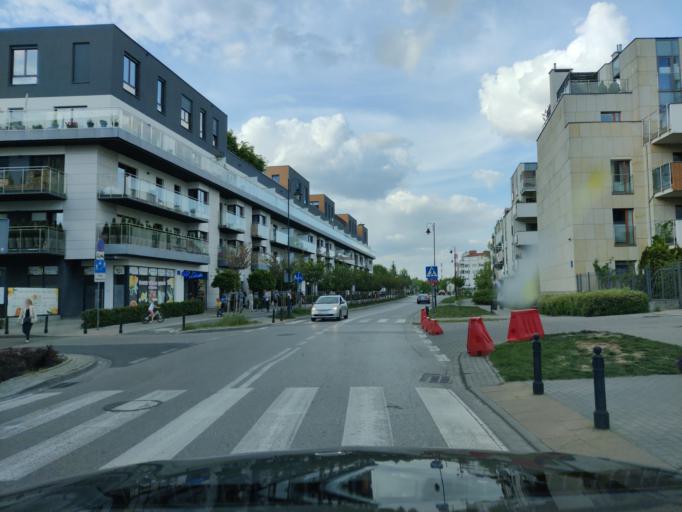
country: PL
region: Masovian Voivodeship
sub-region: Warszawa
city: Wilanow
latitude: 52.1663
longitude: 21.0746
